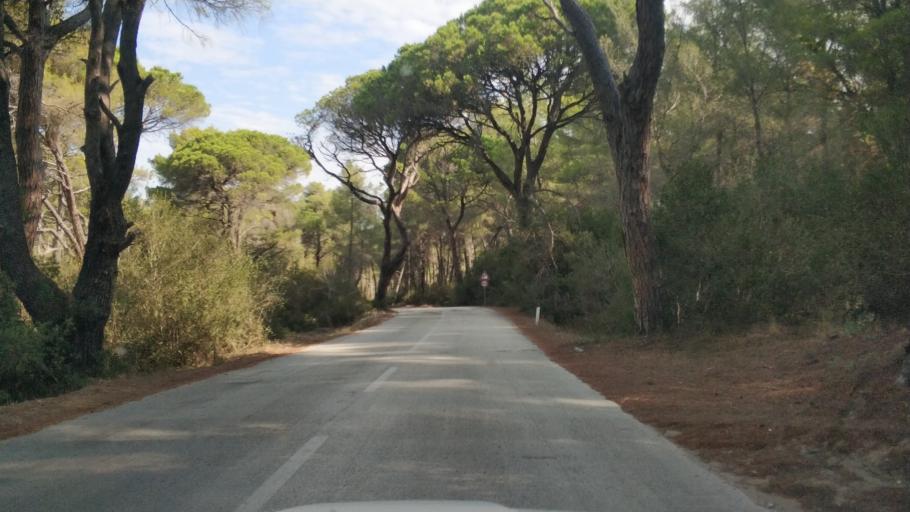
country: AL
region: Fier
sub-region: Rrethi i Lushnjes
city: Divjake
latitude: 40.9846
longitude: 19.4830
